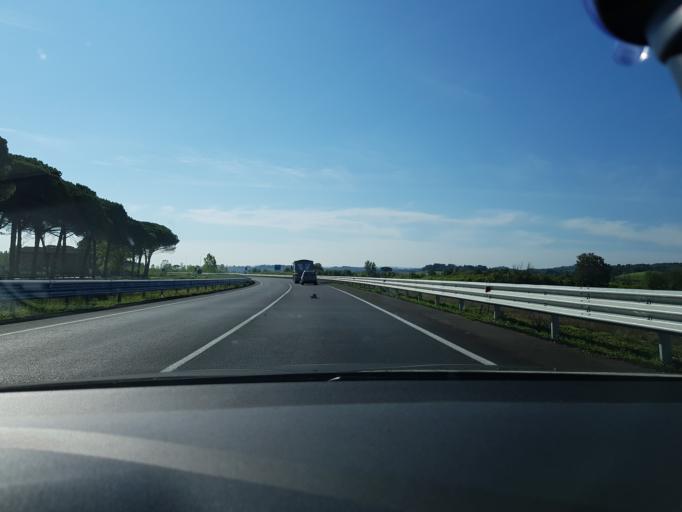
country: IT
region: Tuscany
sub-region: Province of Pisa
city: Ponte A Elsa
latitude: 43.6829
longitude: 10.9130
